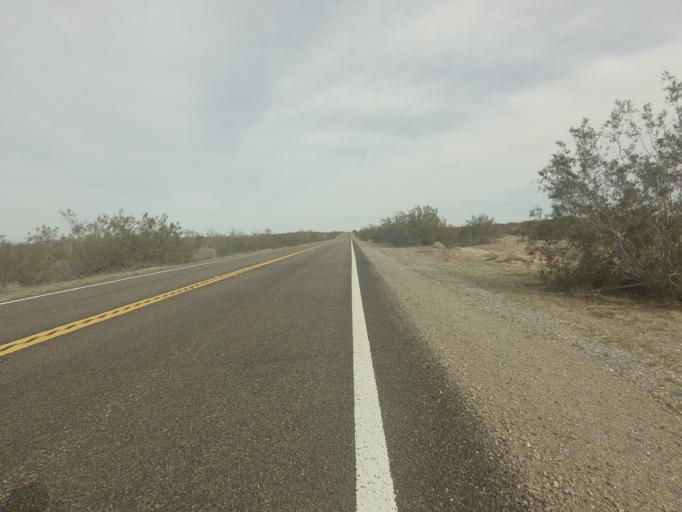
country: US
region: California
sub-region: Imperial County
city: Holtville
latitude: 32.9705
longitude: -115.2563
